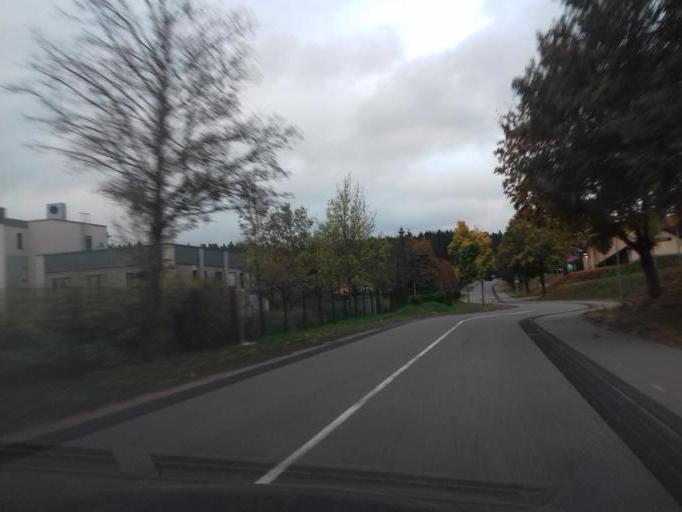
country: DE
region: Rheinland-Pfalz
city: Tawern
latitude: 49.6672
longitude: 6.5248
